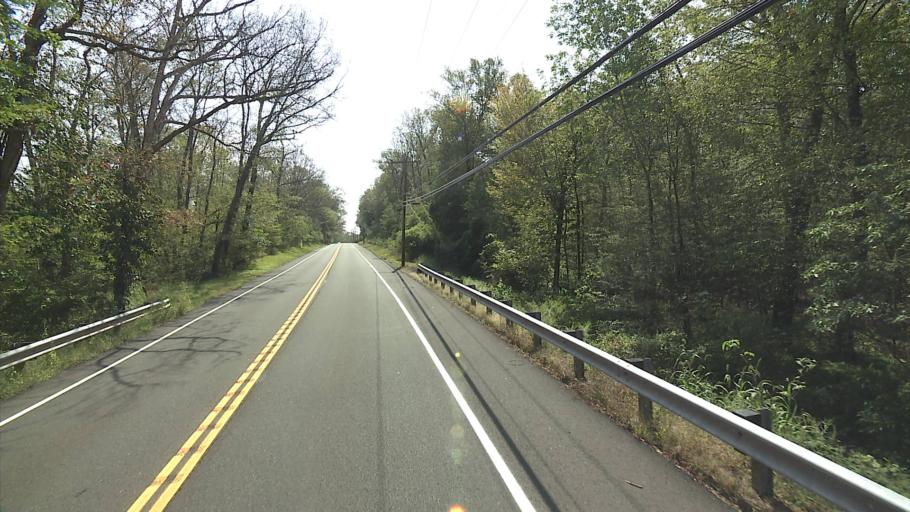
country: US
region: Connecticut
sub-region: Middlesex County
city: Durham
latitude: 41.3860
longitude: -72.6454
